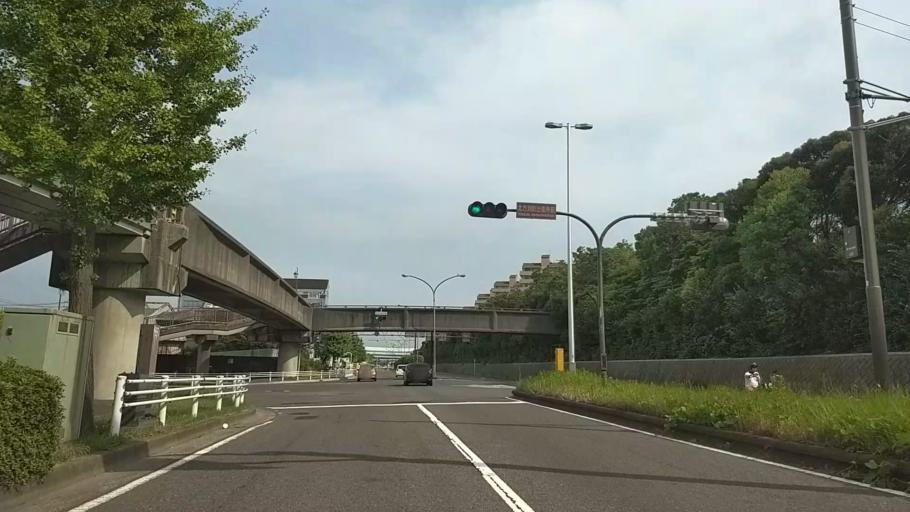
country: JP
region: Kanagawa
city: Yokohama
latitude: 35.4298
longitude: 139.6666
